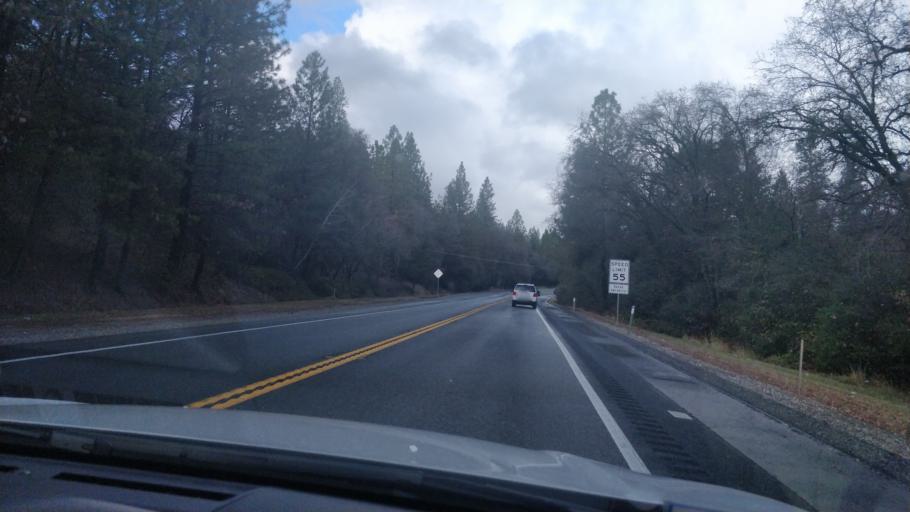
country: US
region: California
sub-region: Nevada County
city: Alta Sierra
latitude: 39.1019
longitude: -121.0853
